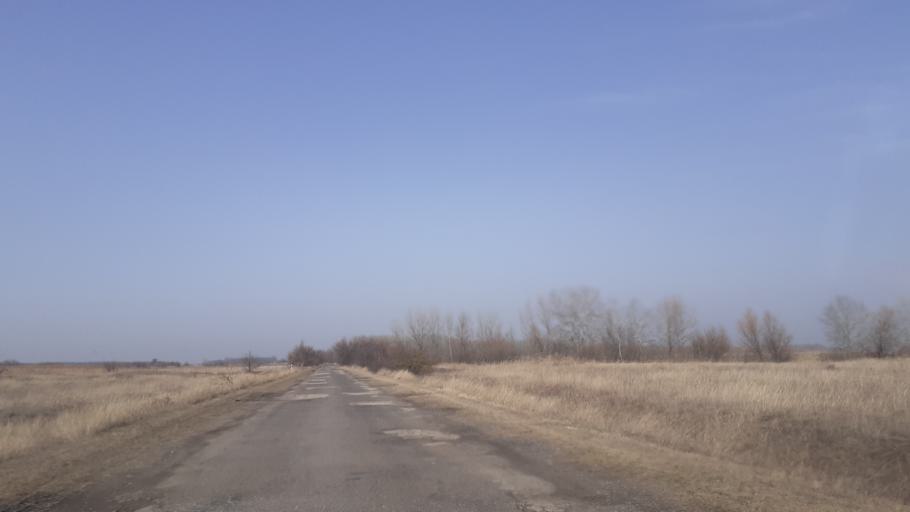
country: HU
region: Pest
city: Dabas
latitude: 47.1056
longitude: 19.2251
